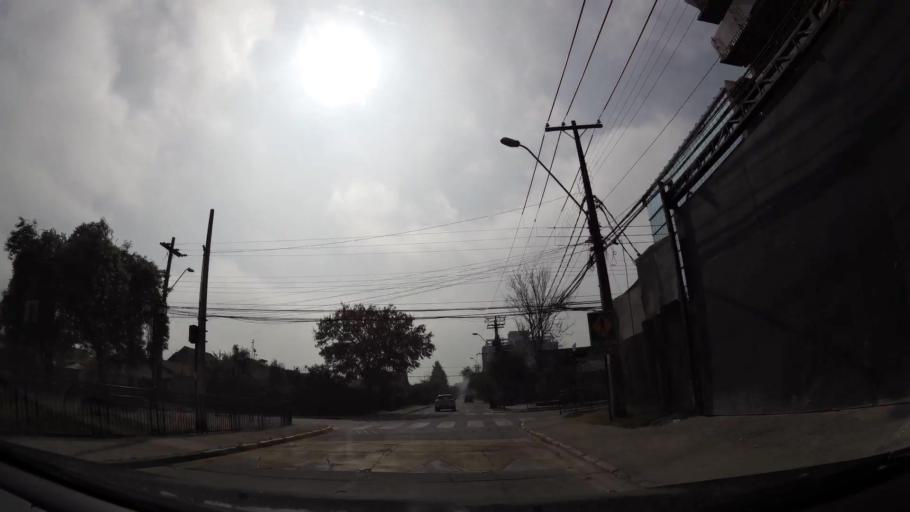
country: CL
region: Santiago Metropolitan
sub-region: Provincia de Santiago
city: Villa Presidente Frei, Nunoa, Santiago, Chile
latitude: -33.3920
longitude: -70.5568
